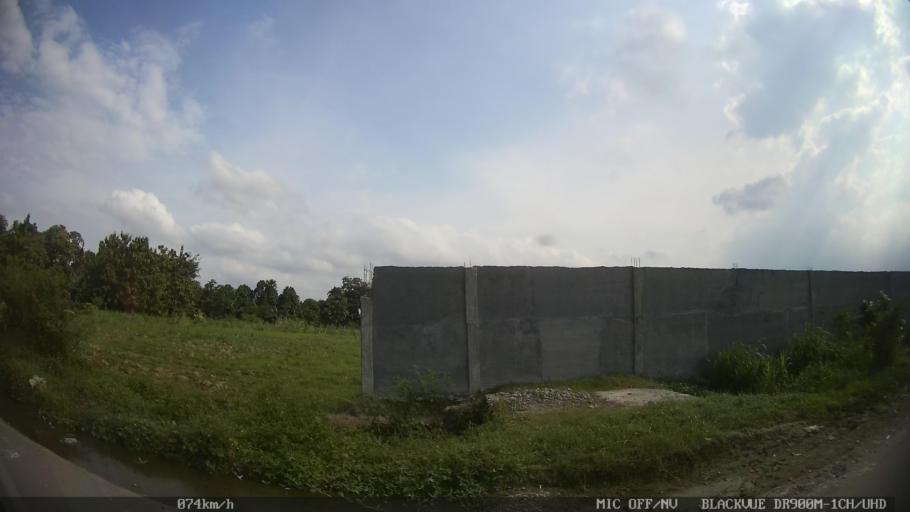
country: ID
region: North Sumatra
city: Percut
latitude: 3.5731
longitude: 98.7756
